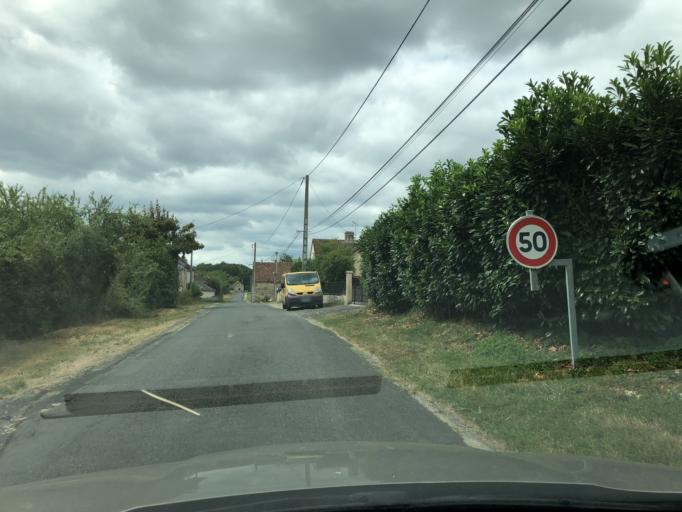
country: FR
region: Centre
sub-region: Departement d'Indre-et-Loire
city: Mazieres-de-Touraine
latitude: 47.3899
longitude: 0.4553
